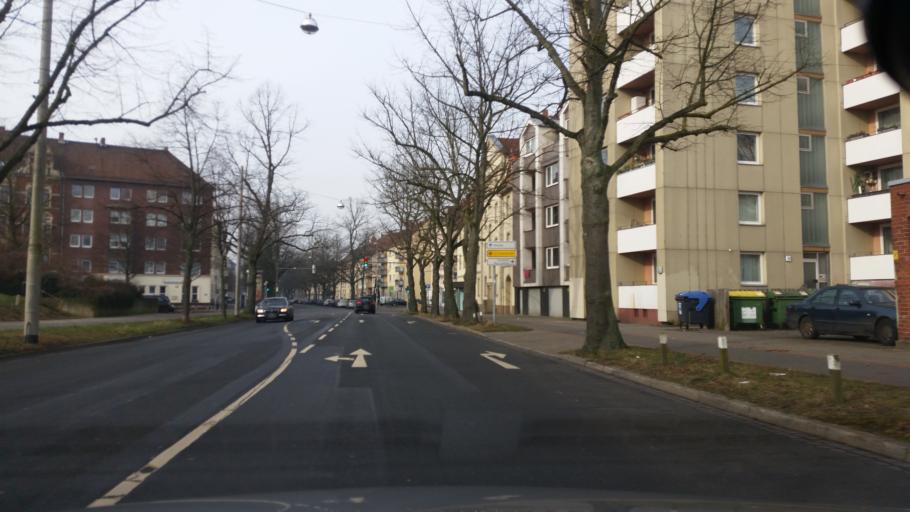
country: DE
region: Lower Saxony
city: Hannover
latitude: 52.3967
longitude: 9.6939
